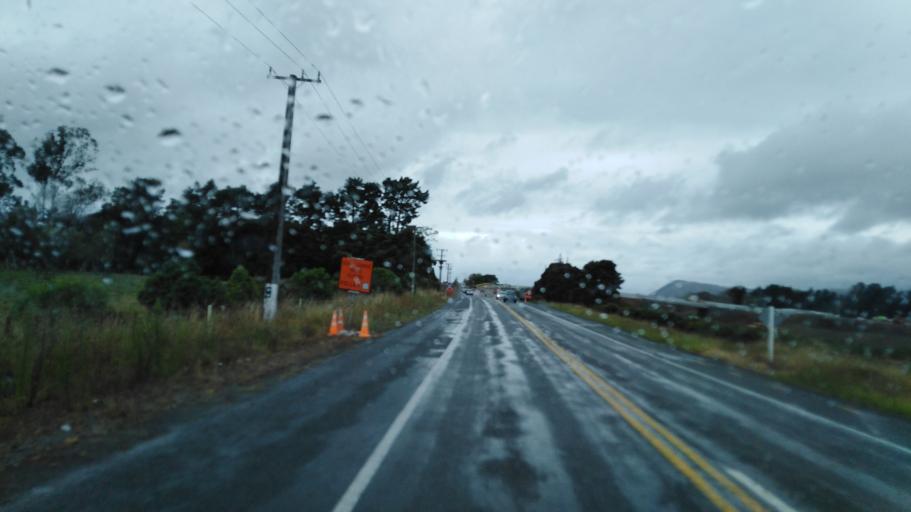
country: NZ
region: Wellington
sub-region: Kapiti Coast District
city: Otaki
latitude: -40.7761
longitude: 175.1412
